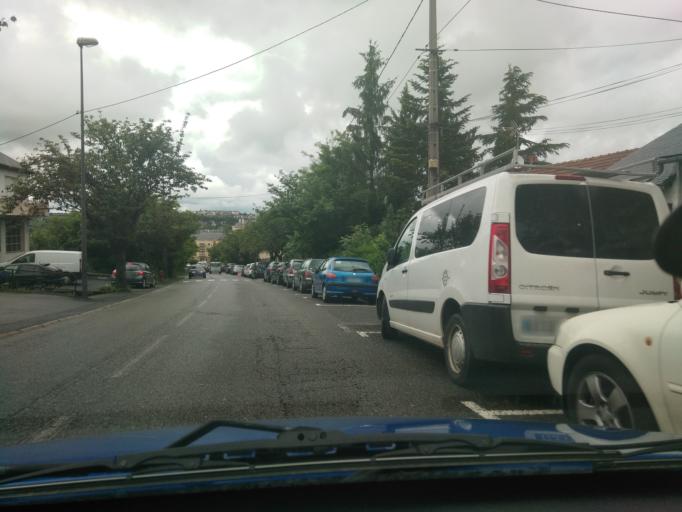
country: FR
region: Midi-Pyrenees
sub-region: Departement de l'Aveyron
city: Rodez
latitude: 44.3592
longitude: 2.5758
